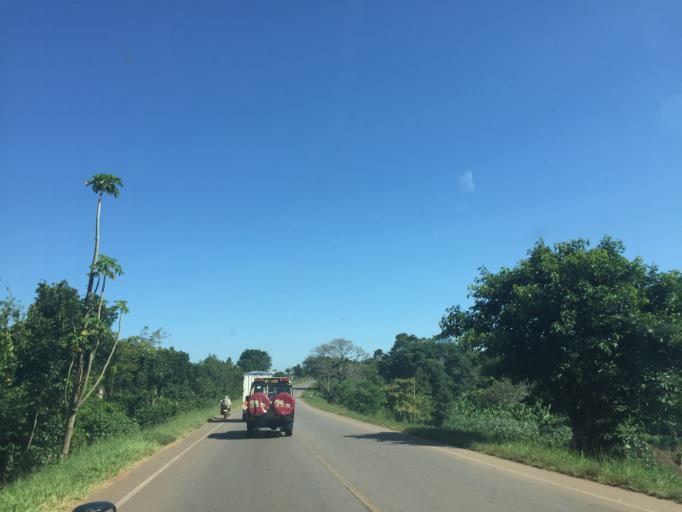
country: UG
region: Central Region
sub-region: Luwero District
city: Wobulenzi
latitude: 0.7591
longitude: 32.5135
